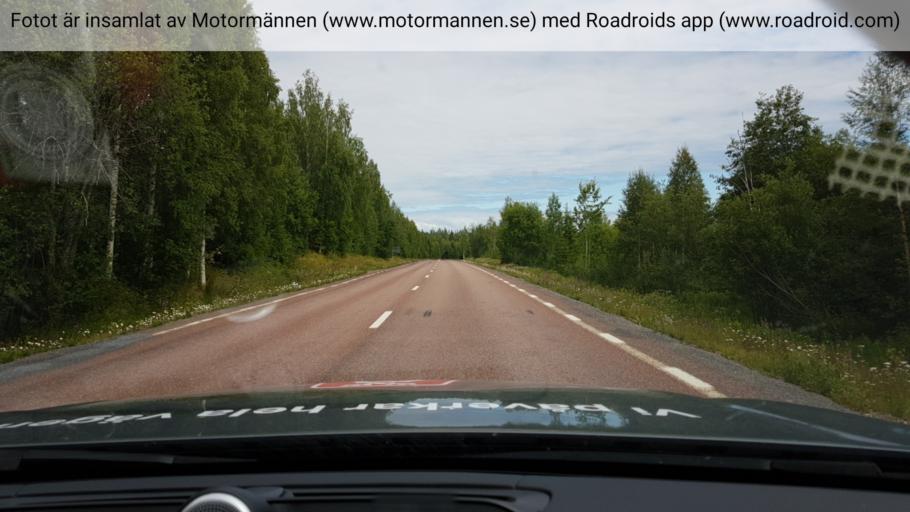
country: SE
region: Jaemtland
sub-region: Stroemsunds Kommun
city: Stroemsund
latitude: 64.0099
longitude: 15.9166
